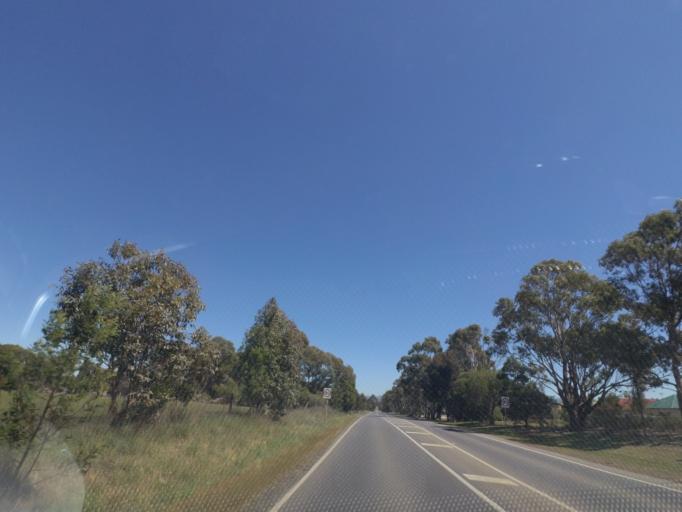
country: AU
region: Victoria
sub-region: Whittlesea
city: Whittlesea
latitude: -37.2943
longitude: 144.9352
